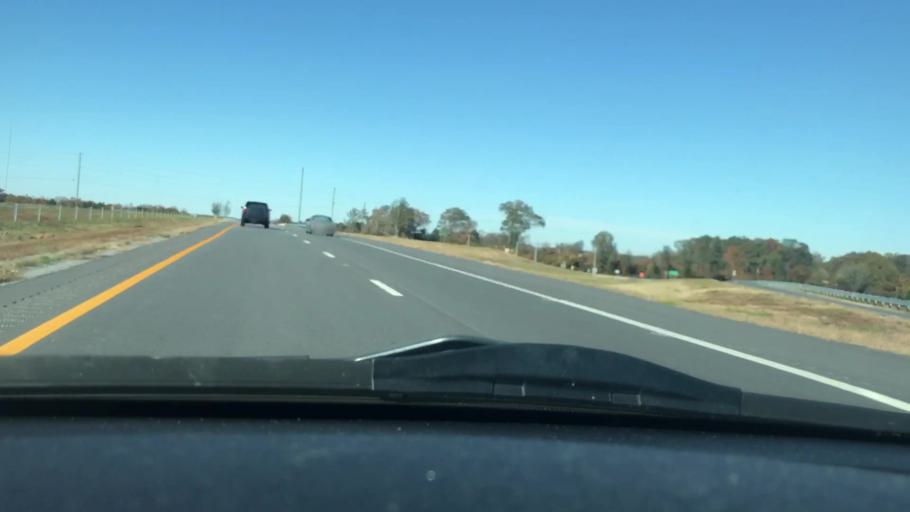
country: US
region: North Carolina
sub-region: Guilford County
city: Summerfield
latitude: 36.2447
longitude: -79.9200
